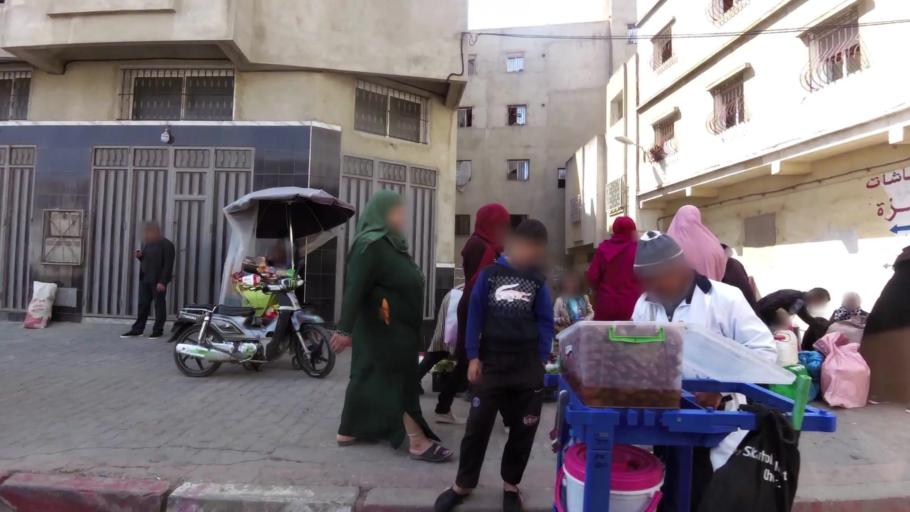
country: MA
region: Tanger-Tetouan
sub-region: Tanger-Assilah
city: Tangier
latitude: 35.7372
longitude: -5.8059
